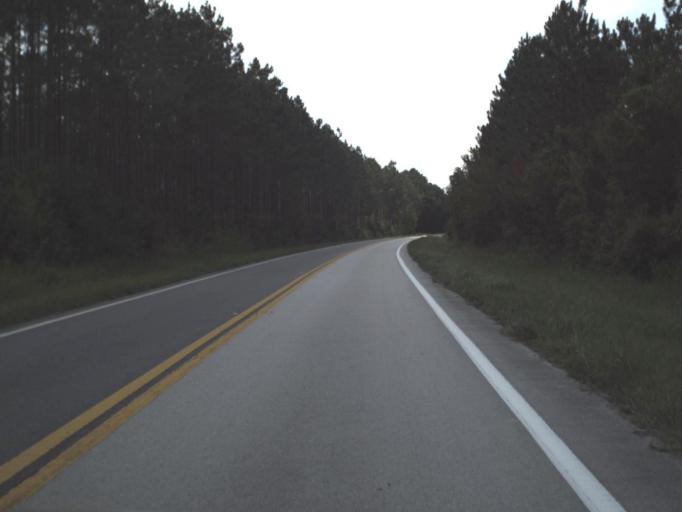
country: US
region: Florida
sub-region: Columbia County
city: Five Points
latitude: 30.5722
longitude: -82.4545
